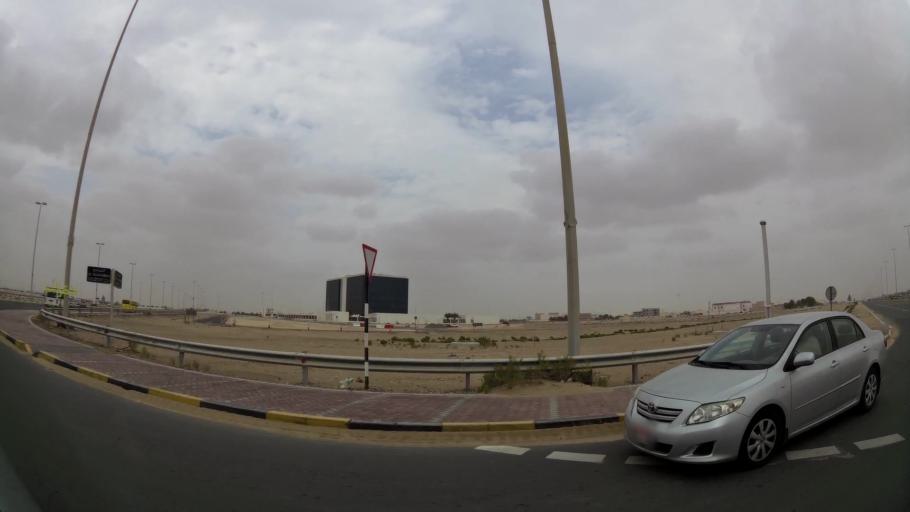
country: AE
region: Abu Dhabi
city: Abu Dhabi
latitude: 24.3367
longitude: 54.6431
